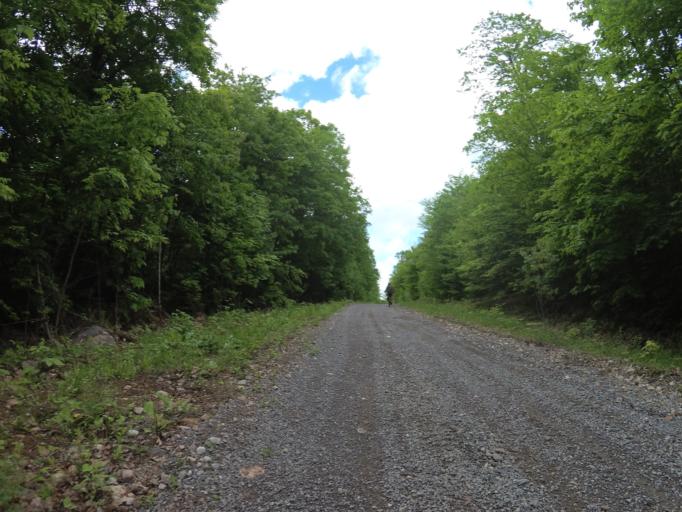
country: CA
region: Ontario
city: Renfrew
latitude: 45.1183
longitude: -76.8851
